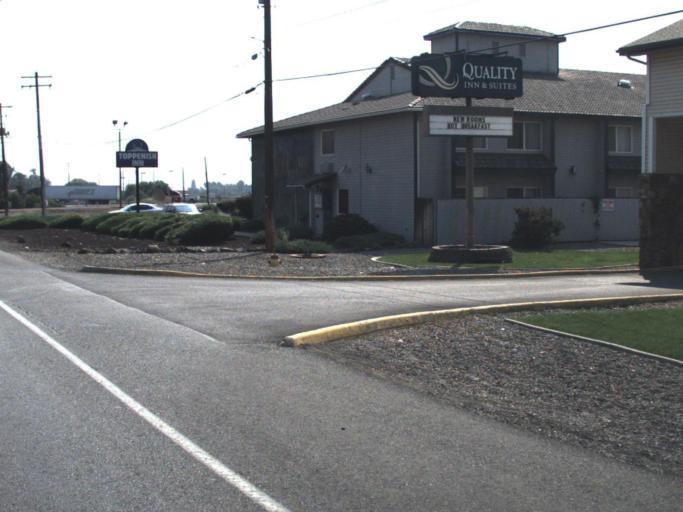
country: US
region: Washington
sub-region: Yakima County
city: Toppenish
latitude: 46.3724
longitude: -120.3203
